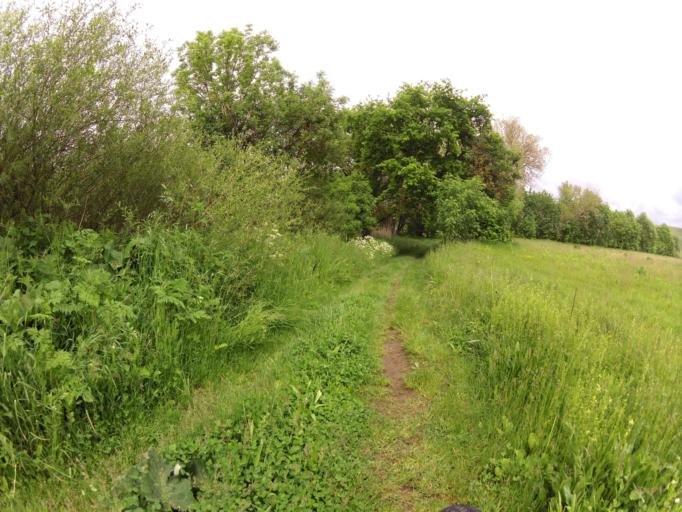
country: DE
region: Bavaria
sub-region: Regierungsbezirk Unterfranken
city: Sommerach
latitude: 49.8300
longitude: 10.1918
